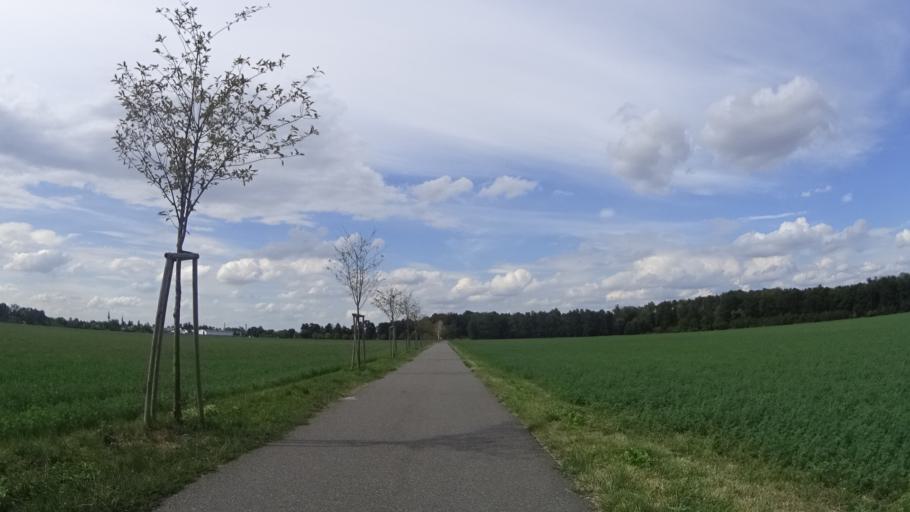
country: CZ
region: Olomoucky
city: Litovel
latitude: 49.6929
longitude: 17.0952
